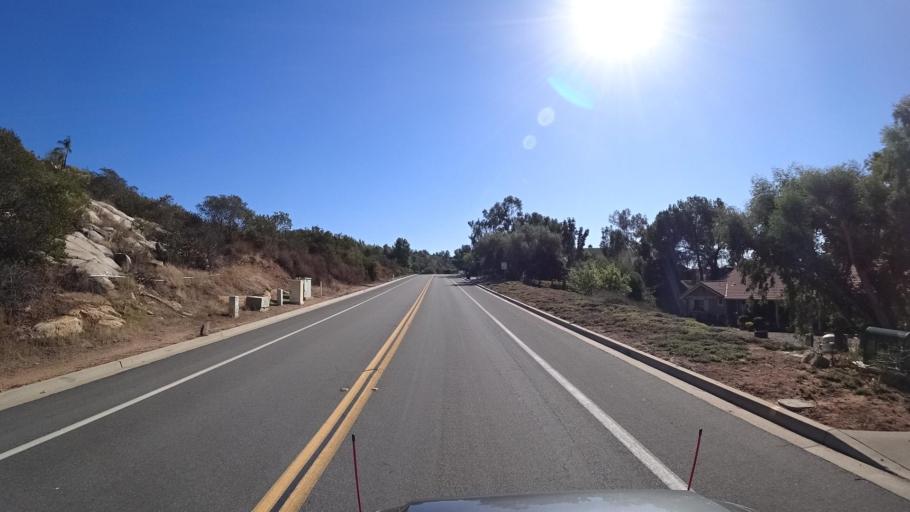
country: US
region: California
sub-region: San Diego County
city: Lakeside
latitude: 32.8626
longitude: -116.8738
